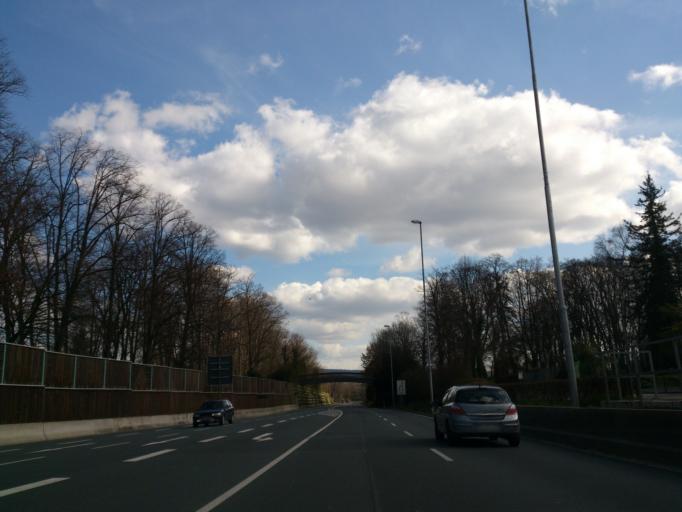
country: DE
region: North Rhine-Westphalia
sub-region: Regierungsbezirk Detmold
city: Hoexter
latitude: 51.7732
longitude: 9.3755
